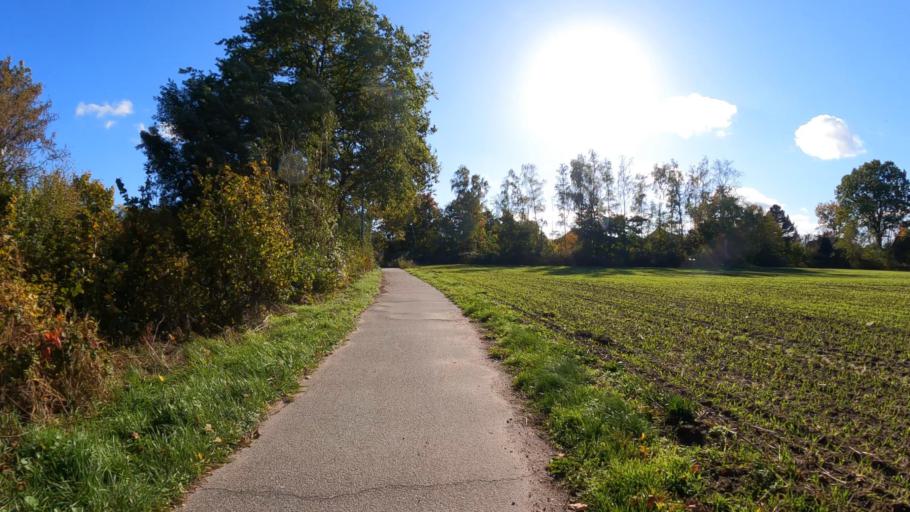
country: DE
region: Schleswig-Holstein
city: Ahrensburg
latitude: 53.6861
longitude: 10.2270
